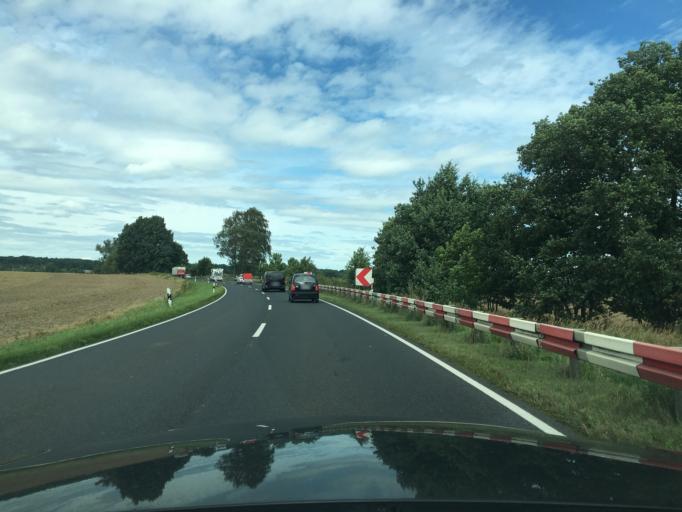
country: DE
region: Brandenburg
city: Gransee
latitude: 53.0471
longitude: 13.1958
